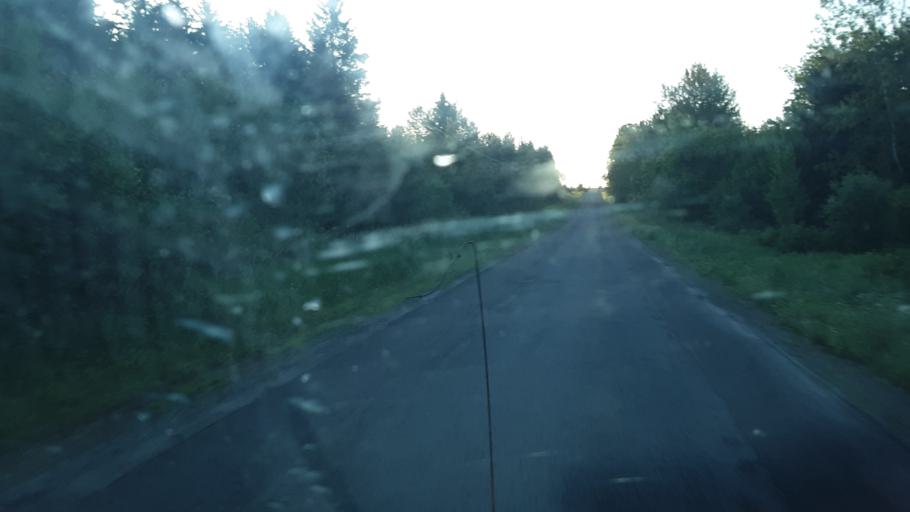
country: US
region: Maine
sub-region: Aroostook County
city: Caribou
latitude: 46.8028
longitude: -68.1077
